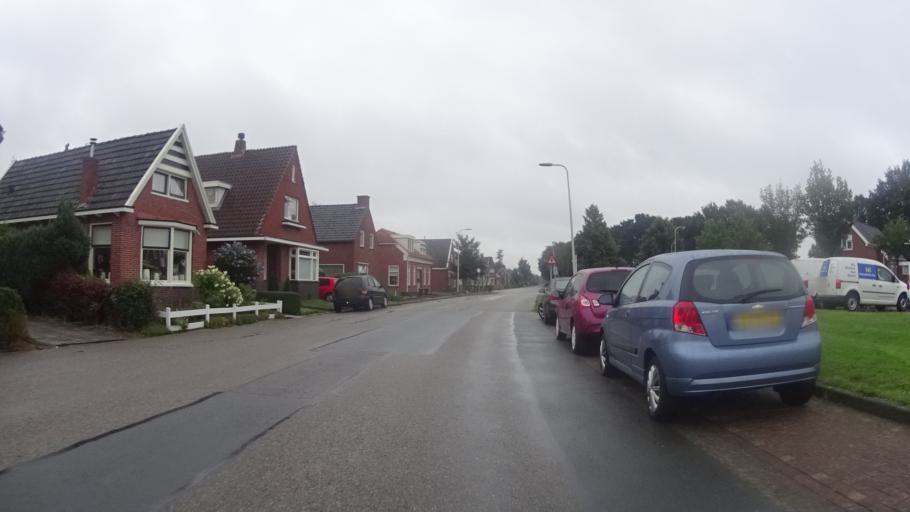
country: NL
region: Groningen
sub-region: Gemeente  Oldambt
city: Winschoten
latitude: 53.1751
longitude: 6.9748
